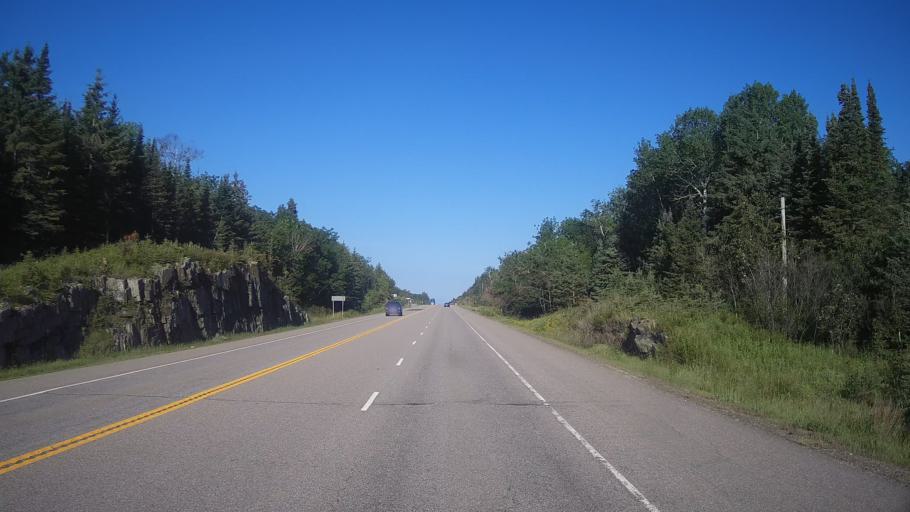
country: US
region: Minnesota
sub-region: Roseau County
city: Warroad
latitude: 49.7186
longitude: -94.7332
